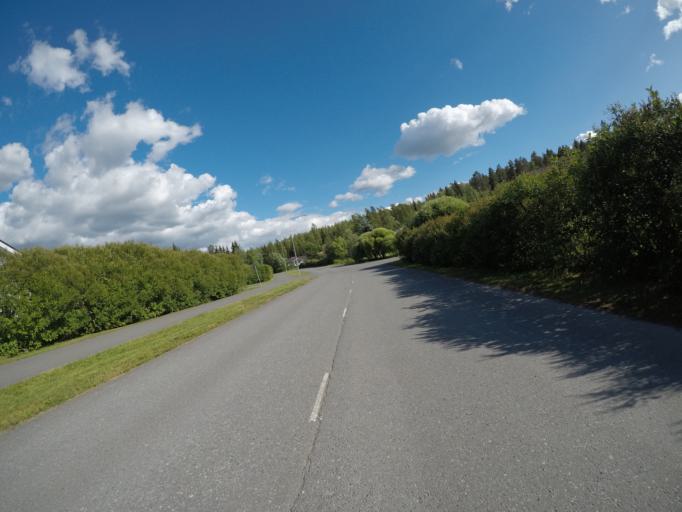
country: FI
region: Haeme
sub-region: Haemeenlinna
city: Haemeenlinna
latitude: 61.0196
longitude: 24.5174
